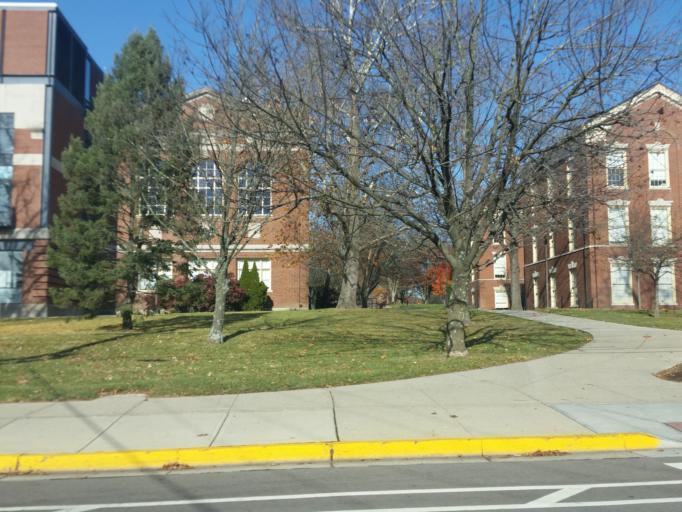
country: US
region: Ohio
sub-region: Butler County
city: Oxford
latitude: 39.5073
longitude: -84.7361
